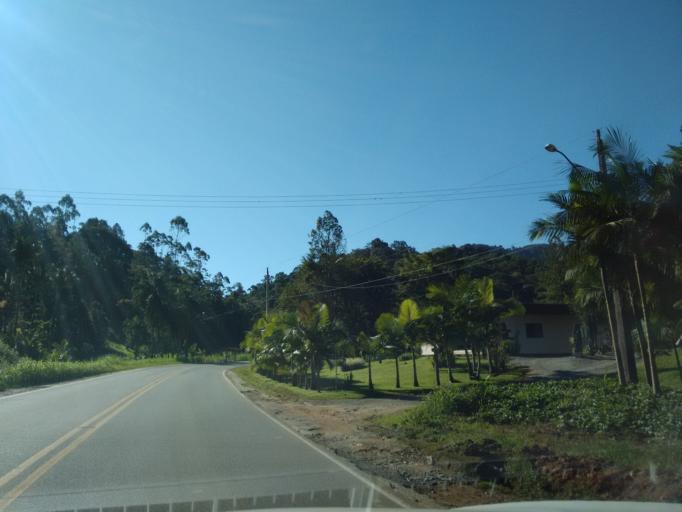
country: BR
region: Santa Catarina
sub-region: Pomerode
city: Pomerode
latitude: -26.6503
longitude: -49.1401
